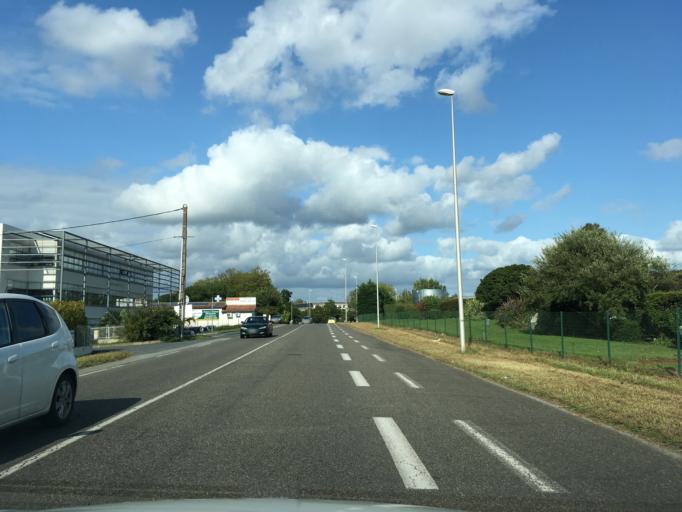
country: FR
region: Aquitaine
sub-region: Departement des Pyrenees-Atlantiques
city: Bayonne
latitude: 43.4689
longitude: -1.4902
